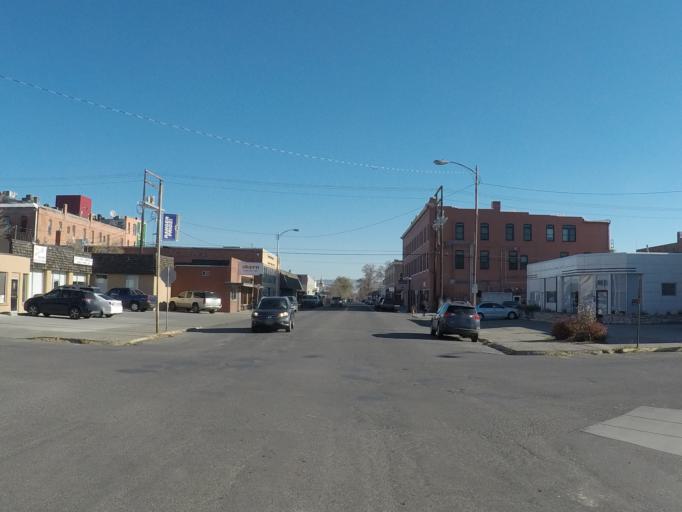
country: US
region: Montana
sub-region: Park County
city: Livingston
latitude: 45.6597
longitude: -110.5602
